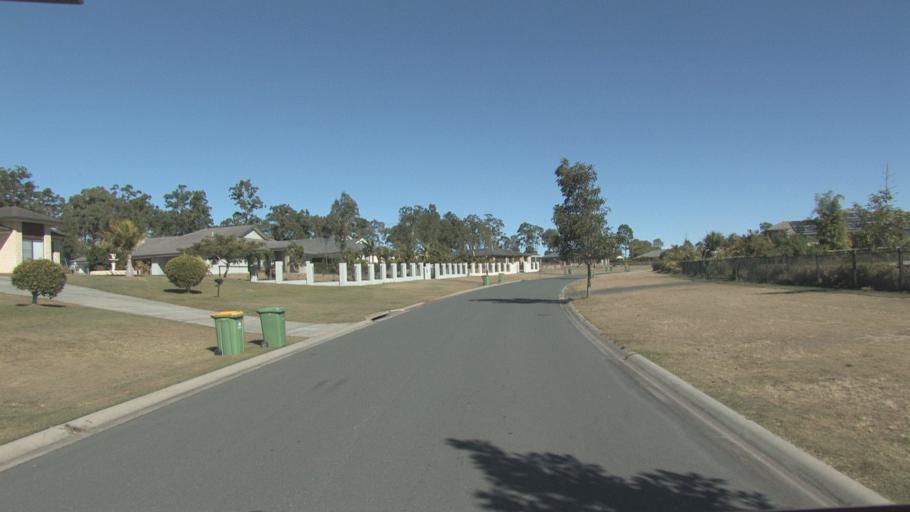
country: AU
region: Queensland
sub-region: Logan
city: North Maclean
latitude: -27.7577
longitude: 152.9487
